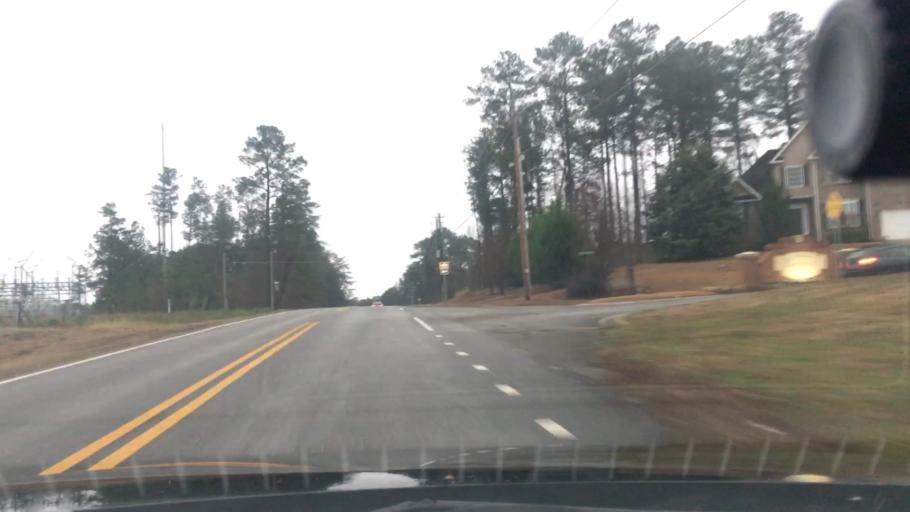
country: US
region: Georgia
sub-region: Bibb County
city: Macon
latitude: 32.9229
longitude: -83.7279
